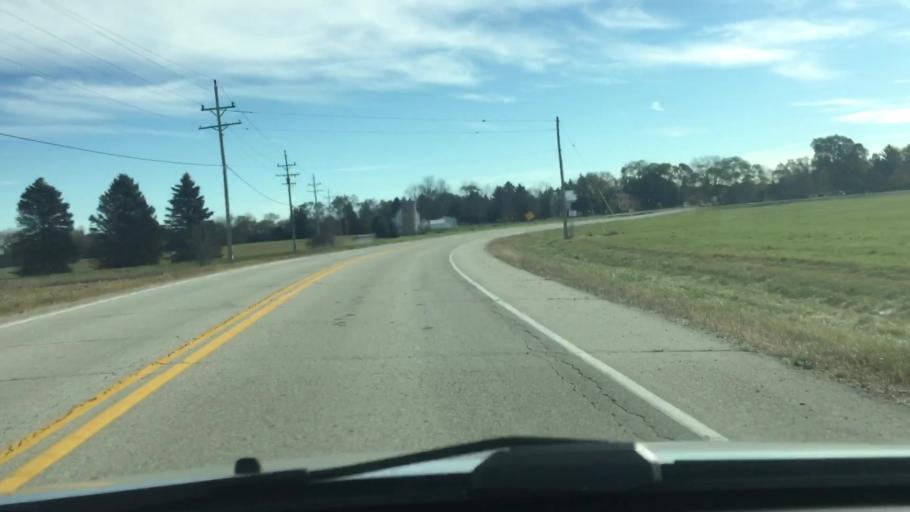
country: US
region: Wisconsin
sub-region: Waukesha County
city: North Prairie
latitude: 42.9448
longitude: -88.3813
